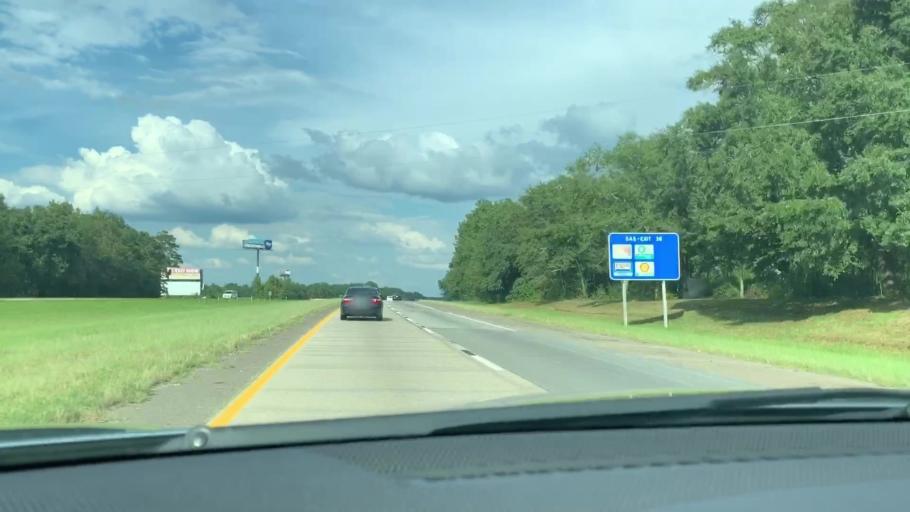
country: US
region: South Carolina
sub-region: Hampton County
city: Yemassee
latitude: 32.6942
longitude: -80.8783
